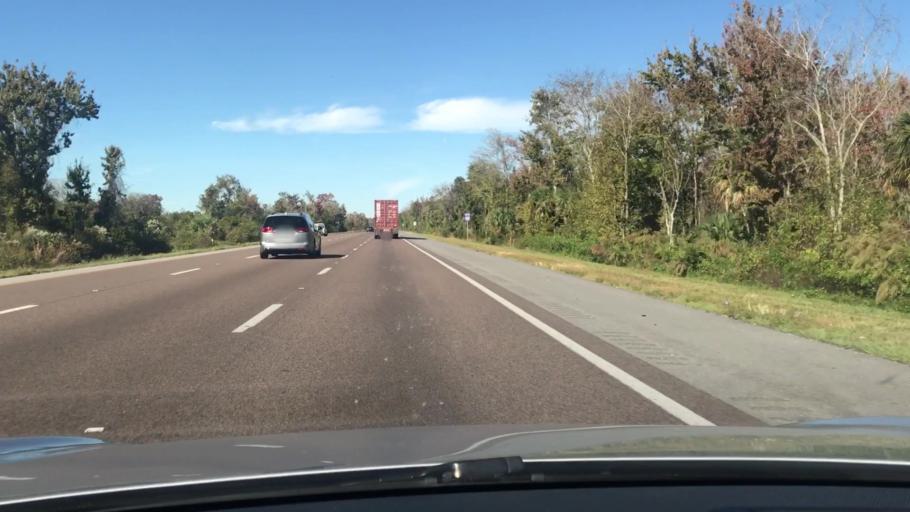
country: US
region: Florida
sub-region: Volusia County
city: Edgewater
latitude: 28.9585
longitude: -80.9539
